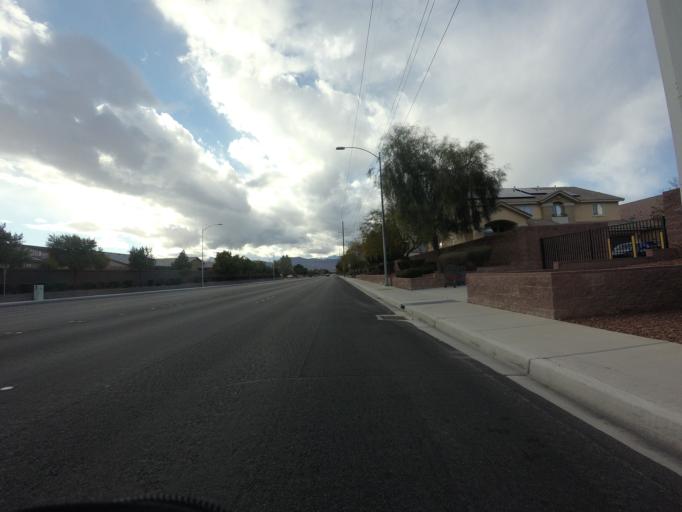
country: US
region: Nevada
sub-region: Clark County
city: North Las Vegas
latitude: 36.2685
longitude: -115.2261
